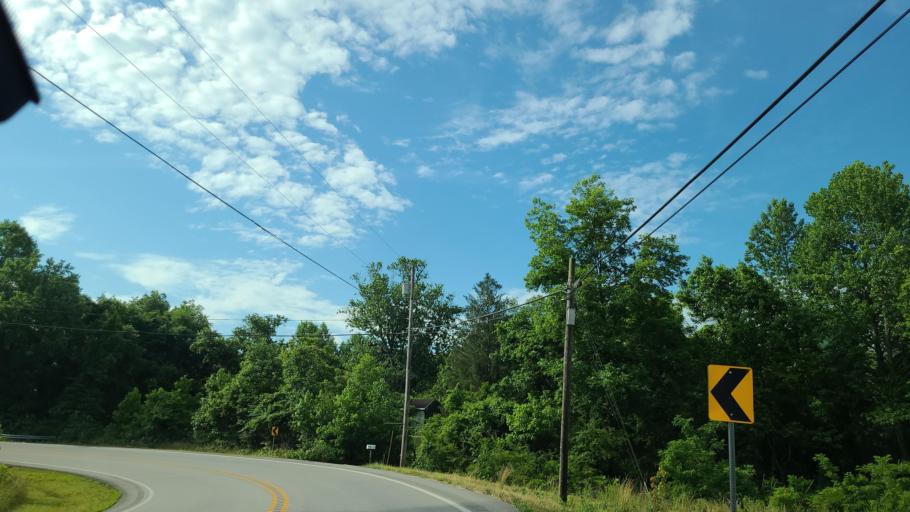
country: US
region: Kentucky
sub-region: Whitley County
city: Williamsburg
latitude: 36.7251
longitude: -84.1281
